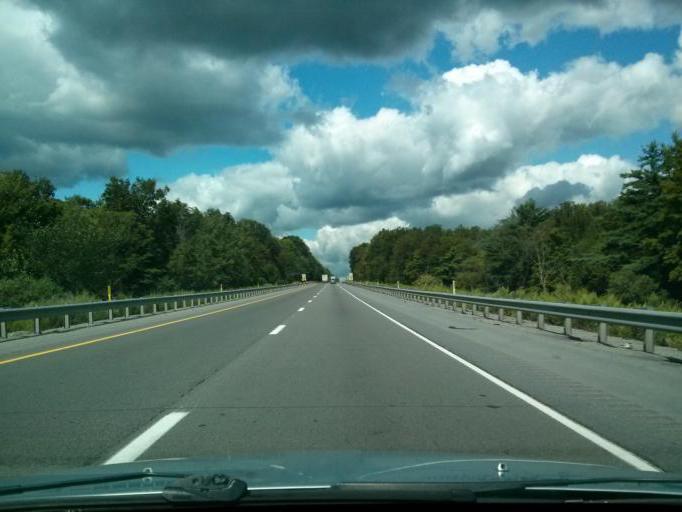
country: US
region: Pennsylvania
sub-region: Clearfield County
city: Treasure Lake
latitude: 41.1323
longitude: -78.7168
